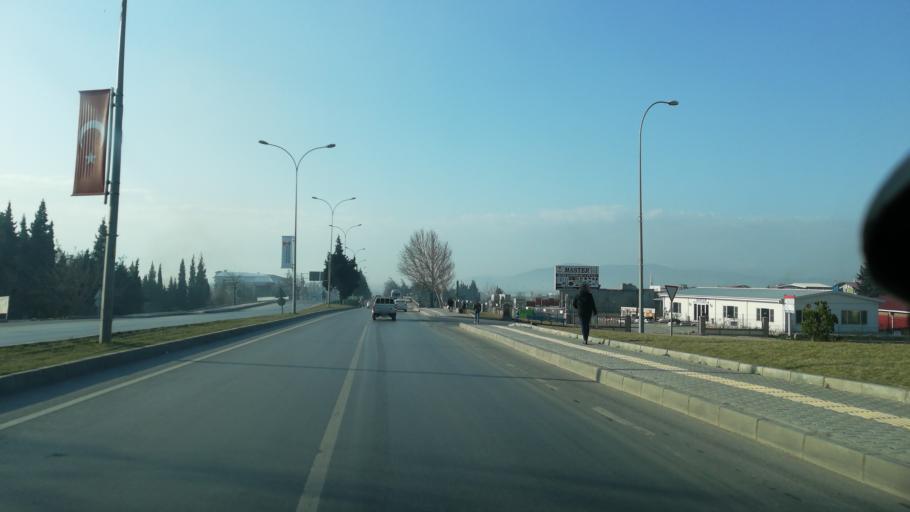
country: TR
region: Kahramanmaras
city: Kahramanmaras
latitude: 37.5674
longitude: 36.9246
